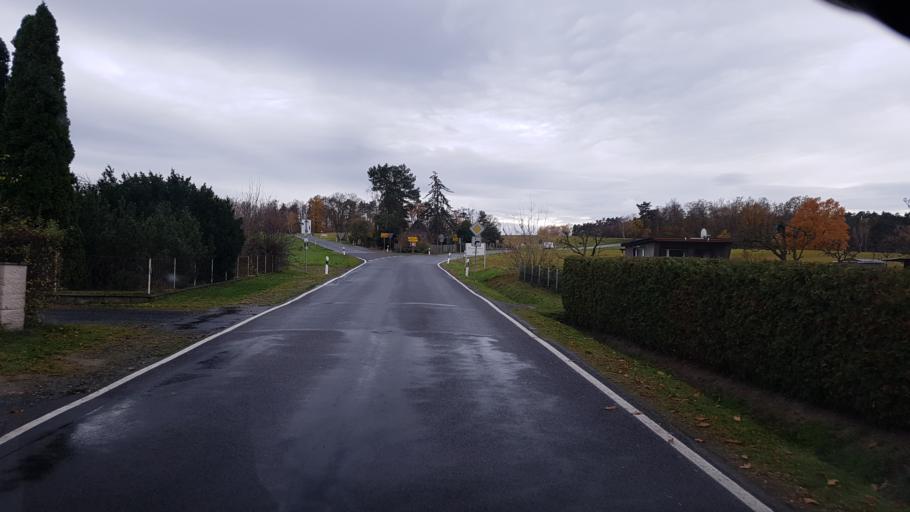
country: DE
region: Brandenburg
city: Ortrand
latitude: 51.3701
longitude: 13.7534
